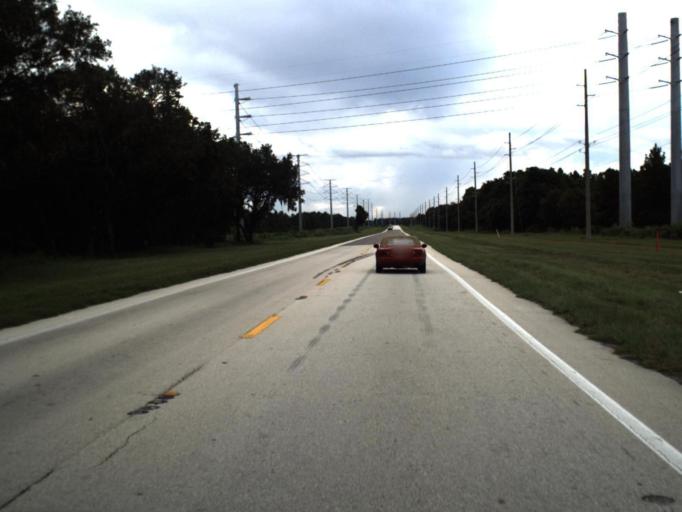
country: US
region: Florida
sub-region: Polk County
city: Mulberry
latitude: 27.7559
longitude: -81.9942
